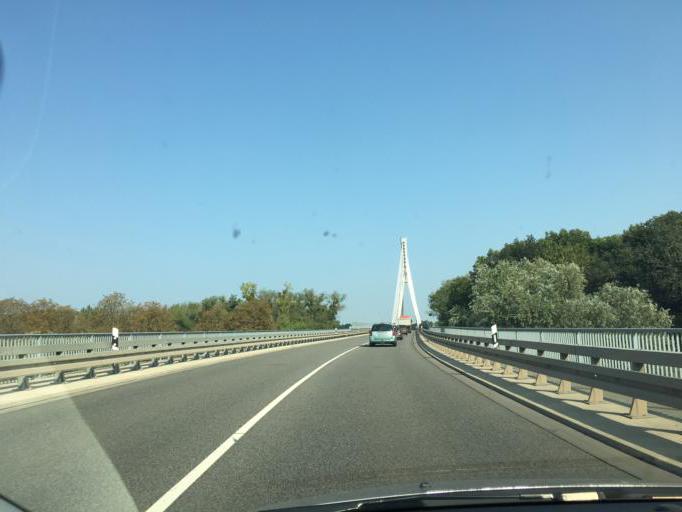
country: DE
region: Saxony-Anhalt
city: Schonebeck
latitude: 52.0192
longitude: 11.7609
